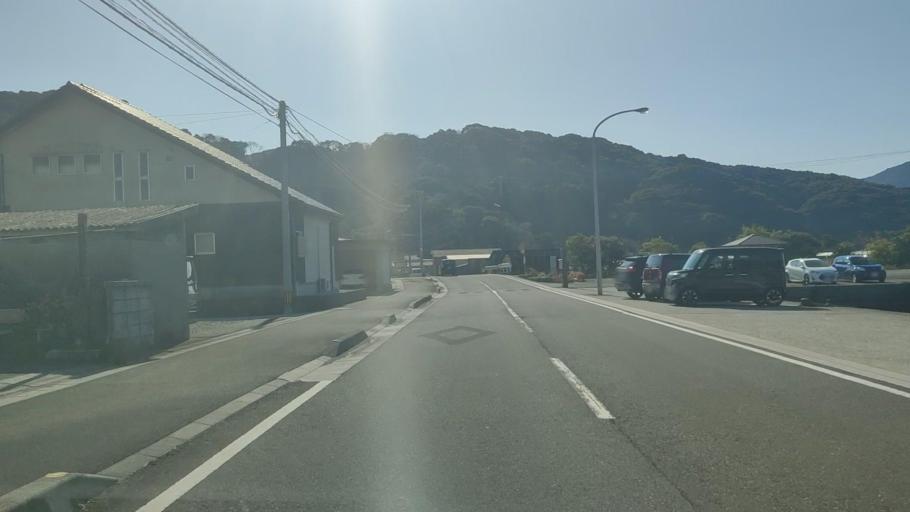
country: JP
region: Oita
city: Saiki
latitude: 32.8008
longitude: 131.9000
